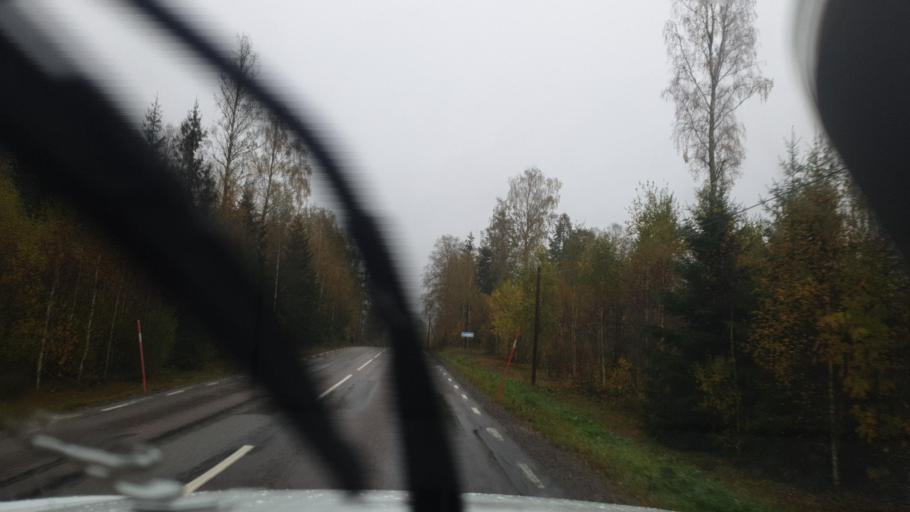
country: SE
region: Vaermland
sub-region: Eda Kommun
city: Amotfors
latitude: 59.7761
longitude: 12.2694
